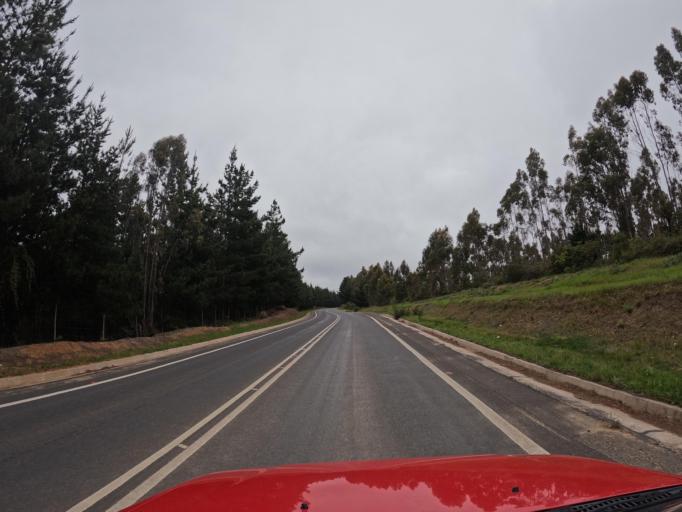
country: CL
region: O'Higgins
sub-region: Provincia de Colchagua
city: Santa Cruz
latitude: -34.6019
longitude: -72.0161
